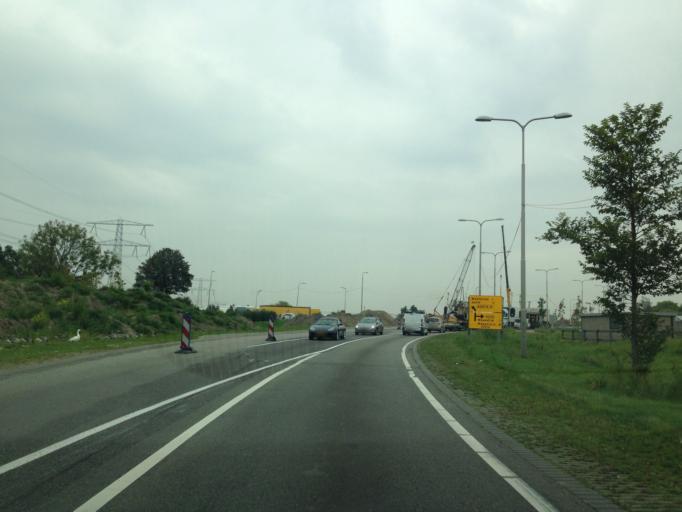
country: NL
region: South Holland
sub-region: Gemeente Westland
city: Maasdijk
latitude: 51.9696
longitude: 4.2013
